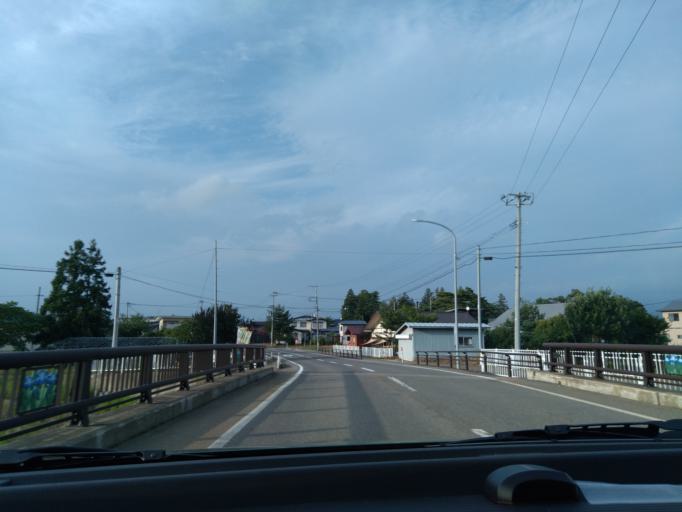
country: JP
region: Akita
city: Yokotemachi
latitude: 39.3834
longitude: 140.5303
